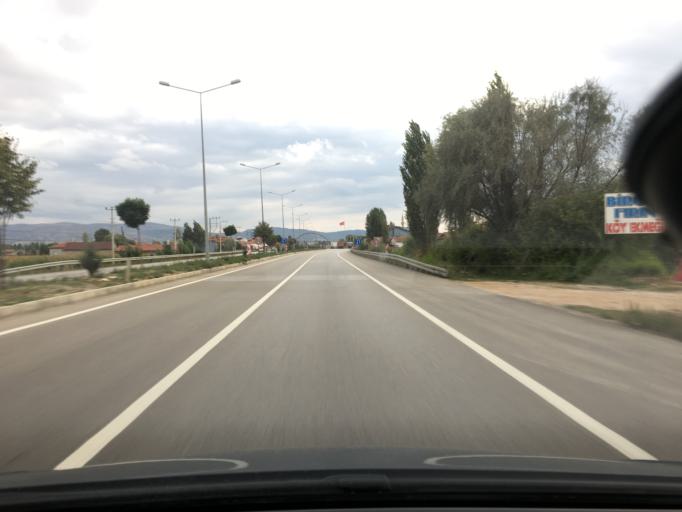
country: TR
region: Afyonkarahisar
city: Sincanli
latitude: 38.7800
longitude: 30.3741
